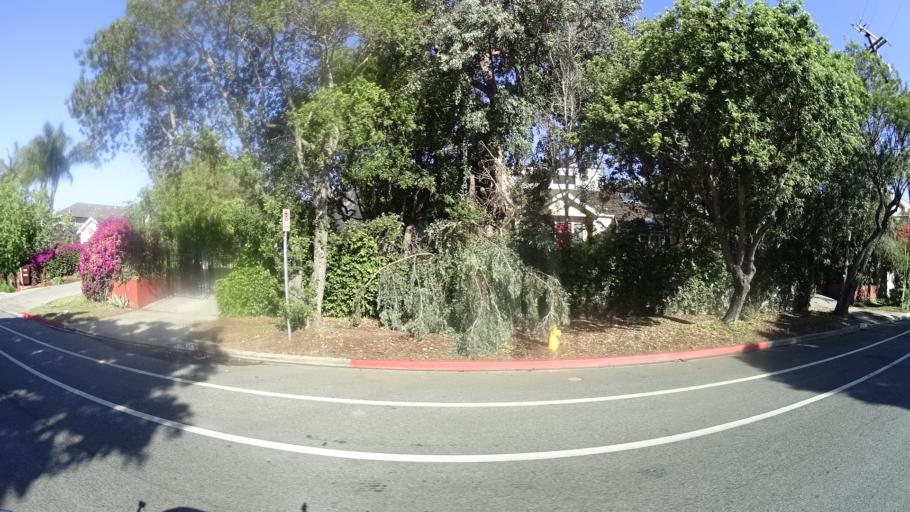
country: US
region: California
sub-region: Los Angeles County
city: Santa Monica
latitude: 34.0341
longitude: -118.5068
